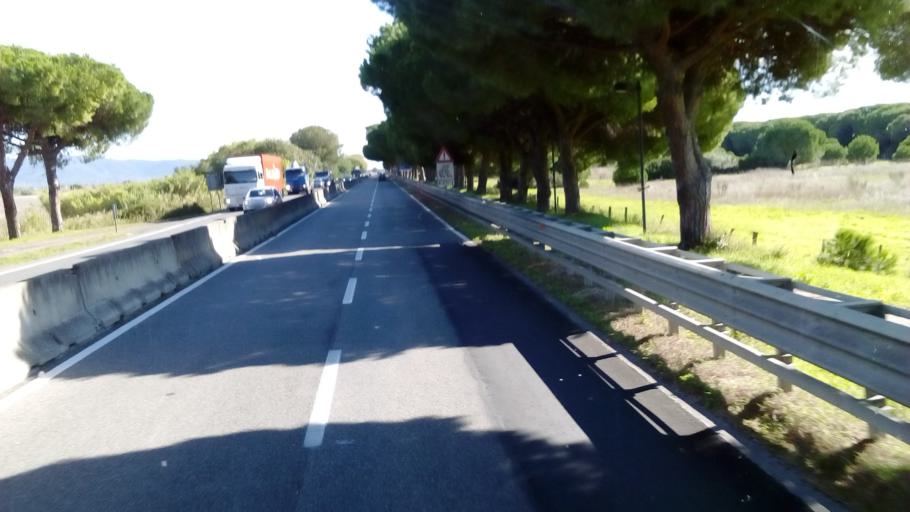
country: IT
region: Tuscany
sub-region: Provincia di Grosseto
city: Fonteblanda
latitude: 42.5422
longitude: 11.1798
